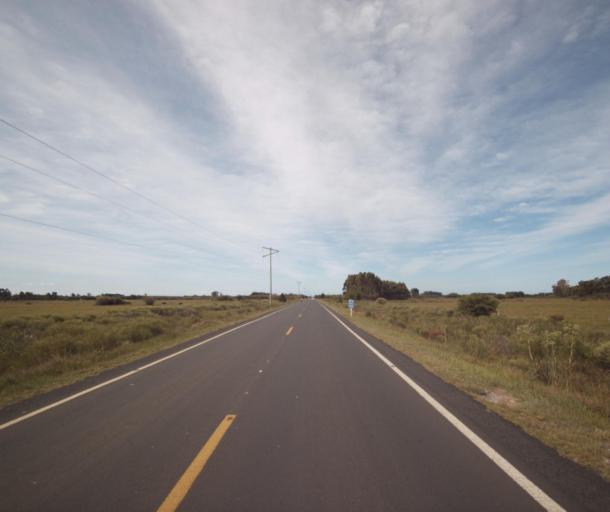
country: BR
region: Rio Grande do Sul
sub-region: Rio Grande
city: Rio Grande
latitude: -31.9248
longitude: -51.9540
